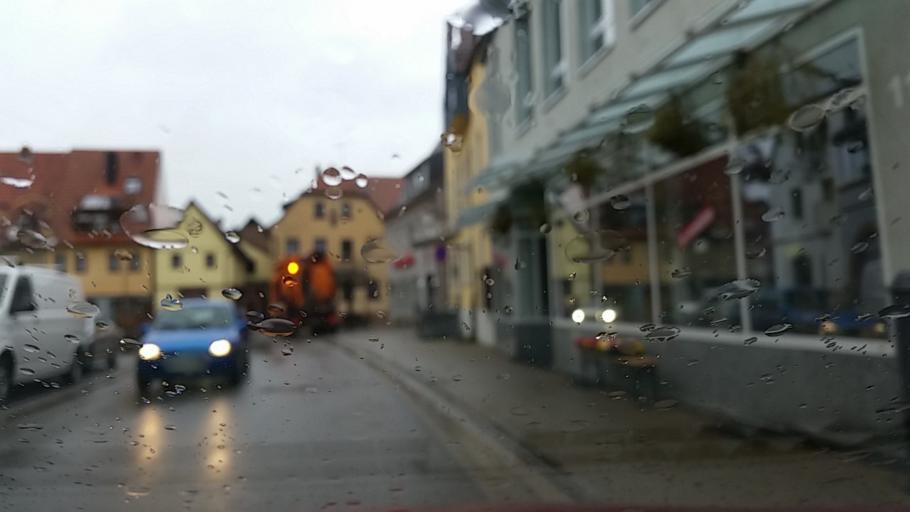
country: DE
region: Bavaria
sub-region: Regierungsbezirk Unterfranken
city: Zellingen
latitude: 49.8987
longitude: 9.8171
